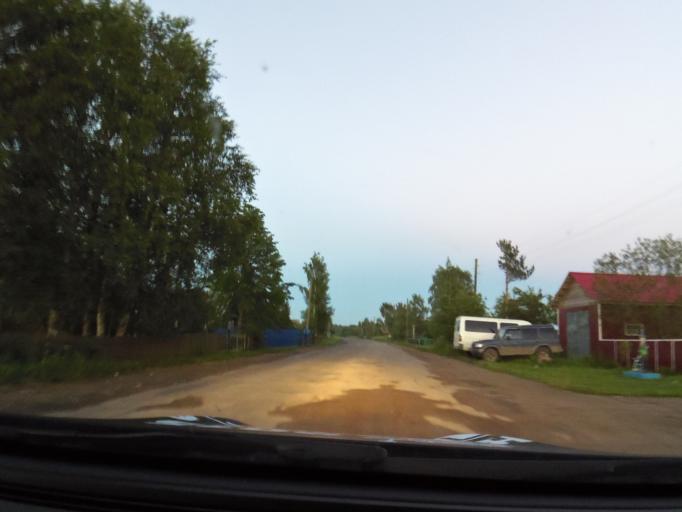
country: RU
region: Vologda
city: Vytegra
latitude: 60.9936
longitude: 36.3450
